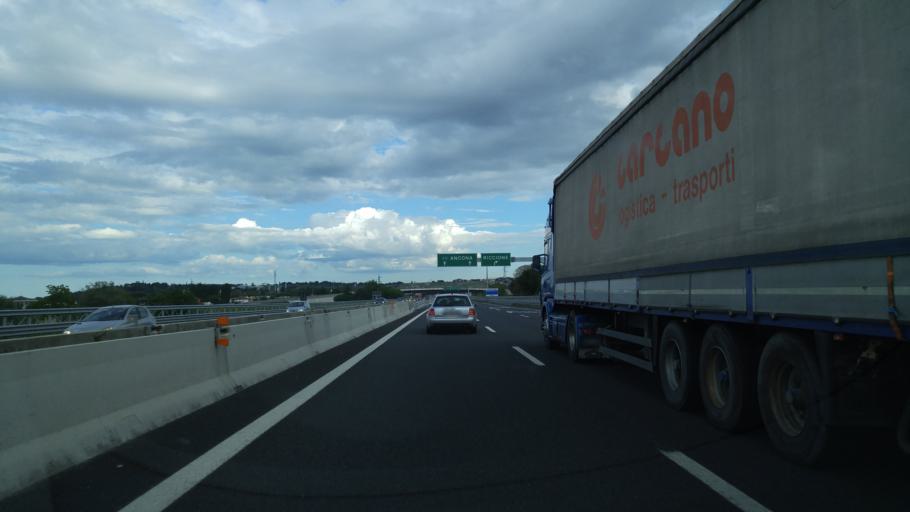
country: IT
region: Emilia-Romagna
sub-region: Provincia di Rimini
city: Riccione
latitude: 43.9901
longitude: 12.6287
